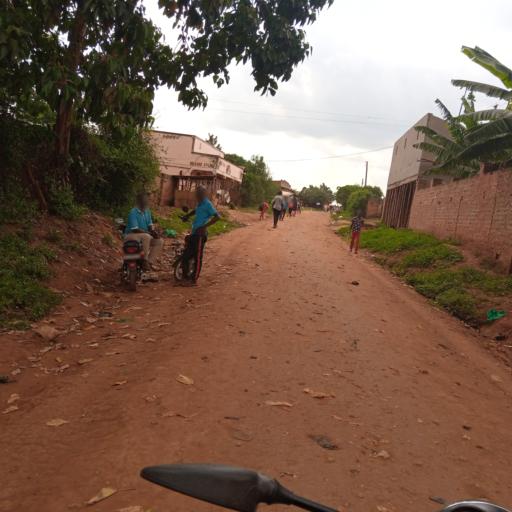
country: UG
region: Eastern Region
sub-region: Mbale District
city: Mbale
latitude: 1.0961
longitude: 34.1774
